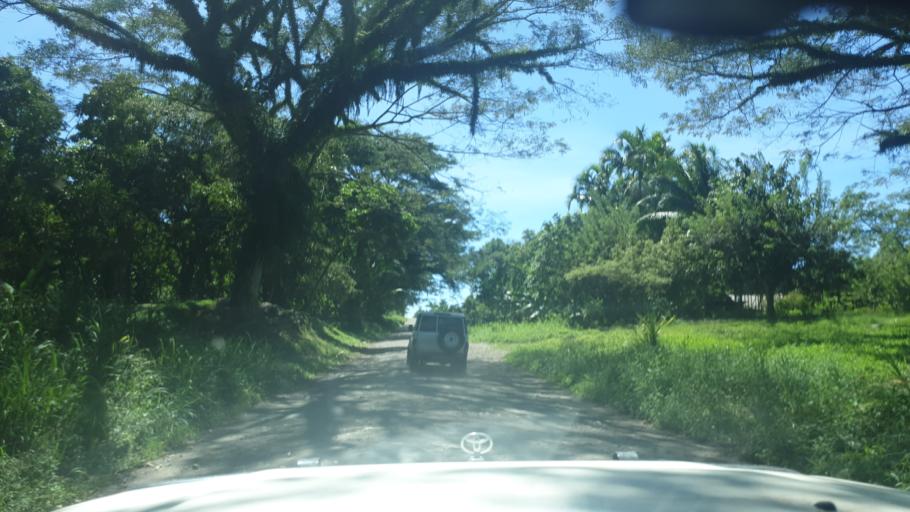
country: PG
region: Bougainville
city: Arawa
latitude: -5.8138
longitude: 155.1486
